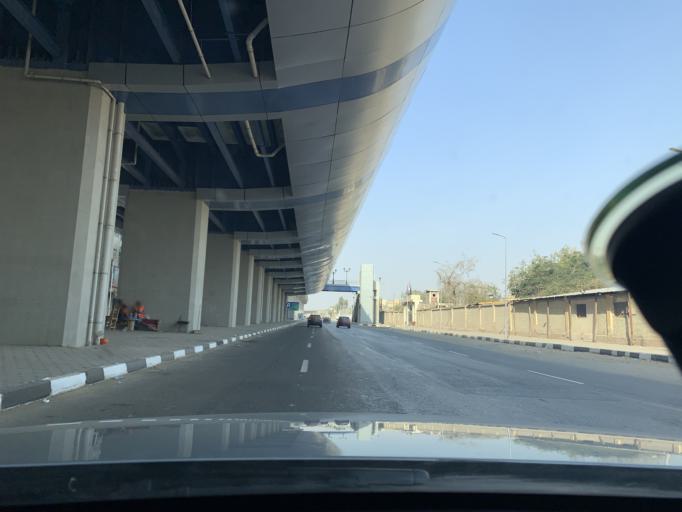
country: EG
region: Muhafazat al Qalyubiyah
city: Al Khankah
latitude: 30.1403
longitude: 31.3940
